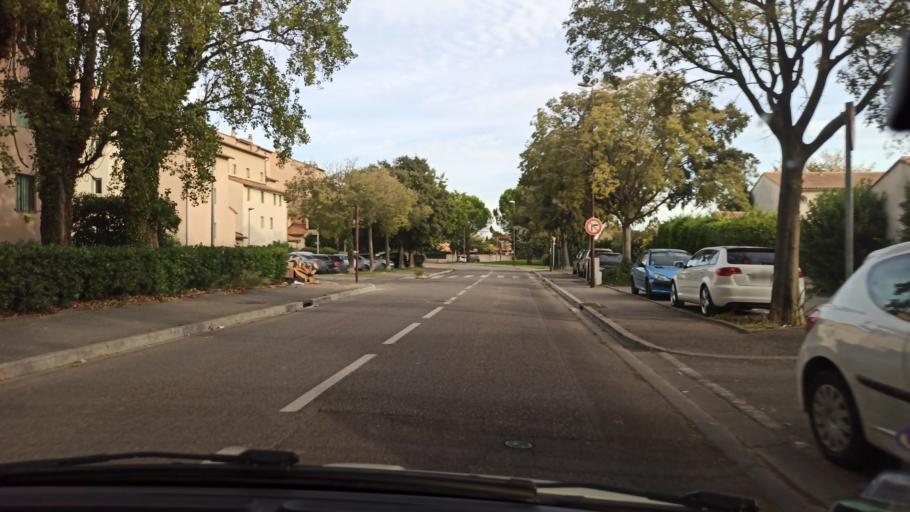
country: FR
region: Provence-Alpes-Cote d'Azur
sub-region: Departement du Vaucluse
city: Le Pontet
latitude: 43.9479
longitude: 4.8460
